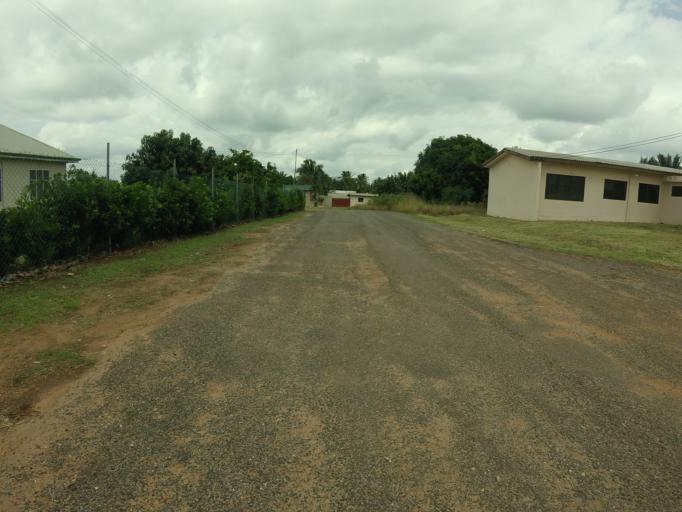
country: GH
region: Volta
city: Ho
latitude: 6.5968
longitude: 0.4839
